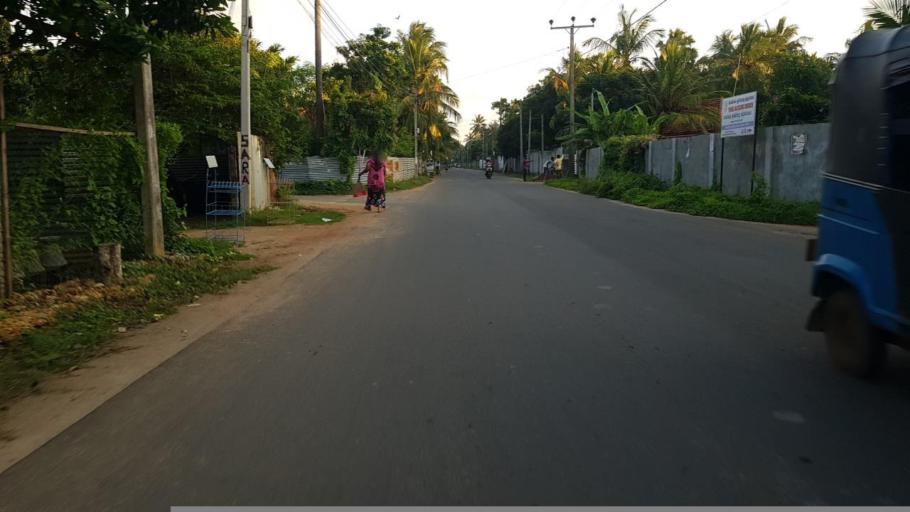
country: LK
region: Northern Province
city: Jaffna
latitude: 9.7156
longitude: 79.9846
